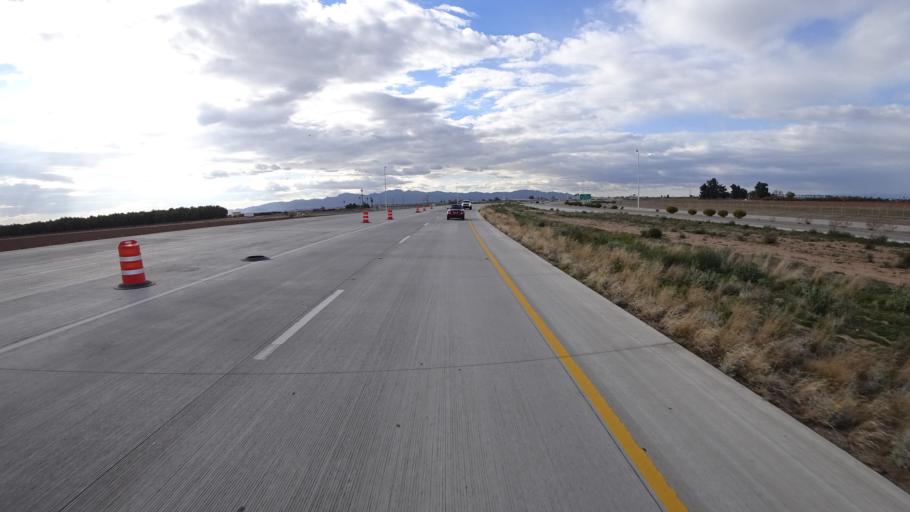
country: US
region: Arizona
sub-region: Maricopa County
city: Litchfield Park
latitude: 33.5510
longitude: -112.3479
